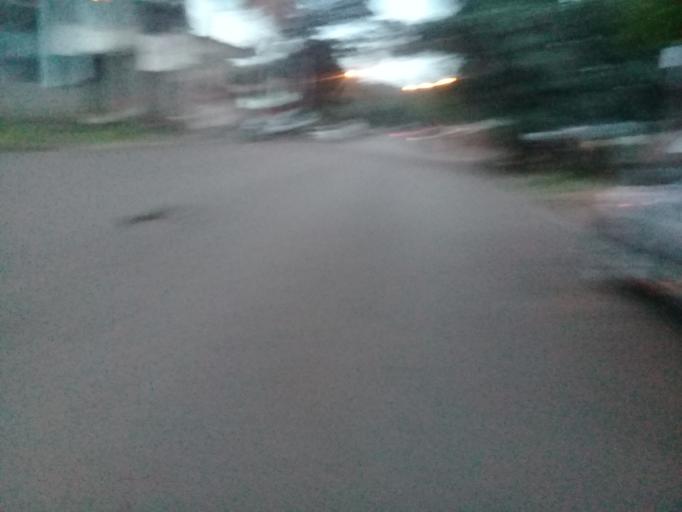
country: AR
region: Misiones
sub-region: Departamento de Iguazu
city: Puerto Iguazu
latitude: -25.5963
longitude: -54.5707
